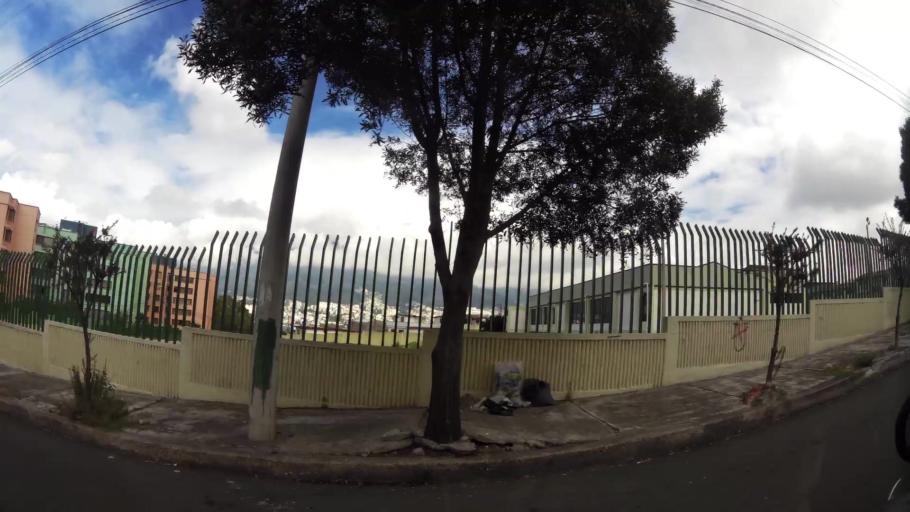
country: EC
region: Pichincha
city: Quito
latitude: -0.1602
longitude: -78.4697
